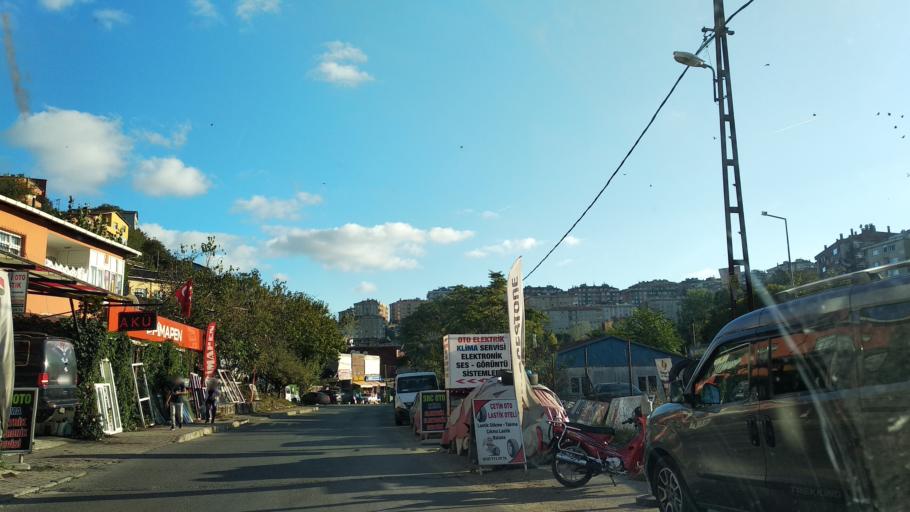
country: TR
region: Istanbul
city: Sisli
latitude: 41.1284
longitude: 29.0381
